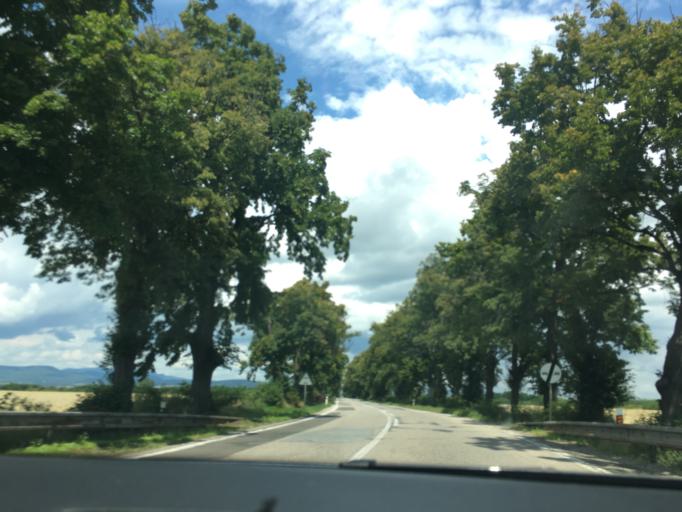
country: HU
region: Borsod-Abauj-Zemplen
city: Satoraljaujhely
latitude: 48.4462
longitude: 21.6528
